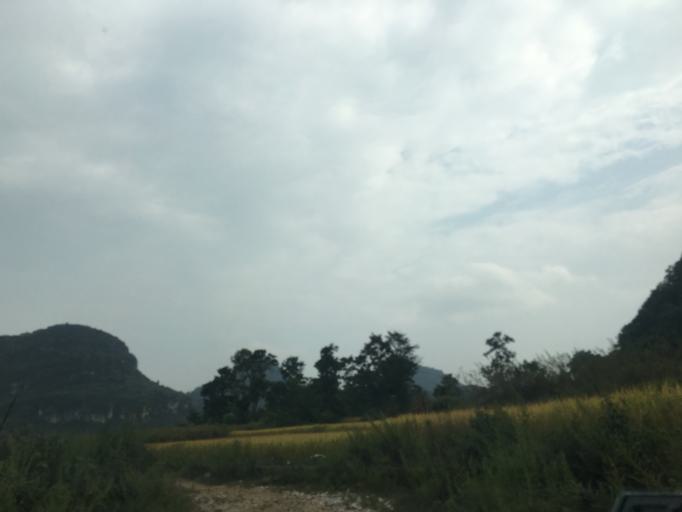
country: CN
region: Guangxi Zhuangzu Zizhiqu
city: Xinzhou
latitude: 25.4948
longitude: 105.6508
